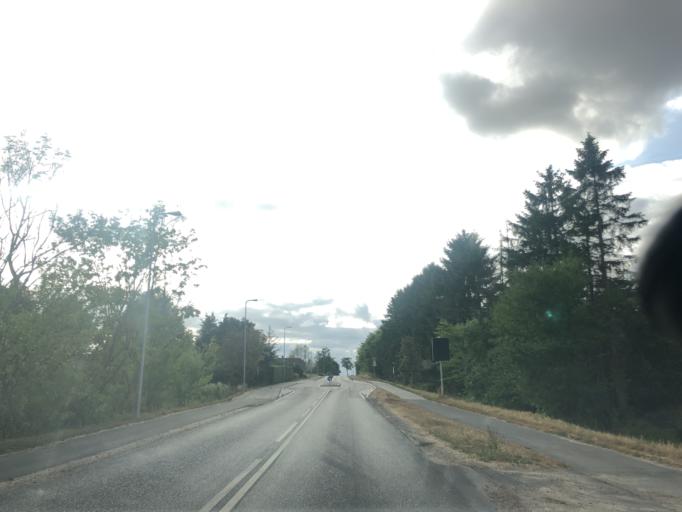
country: DK
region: Zealand
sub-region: Koge Kommune
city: Bjaeverskov
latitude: 55.4281
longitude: 11.9855
